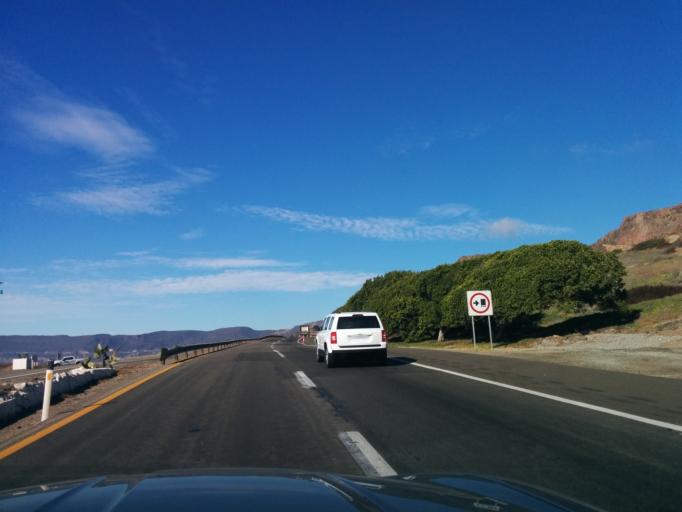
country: MX
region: Baja California
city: El Sauzal
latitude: 31.9222
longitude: -116.7519
